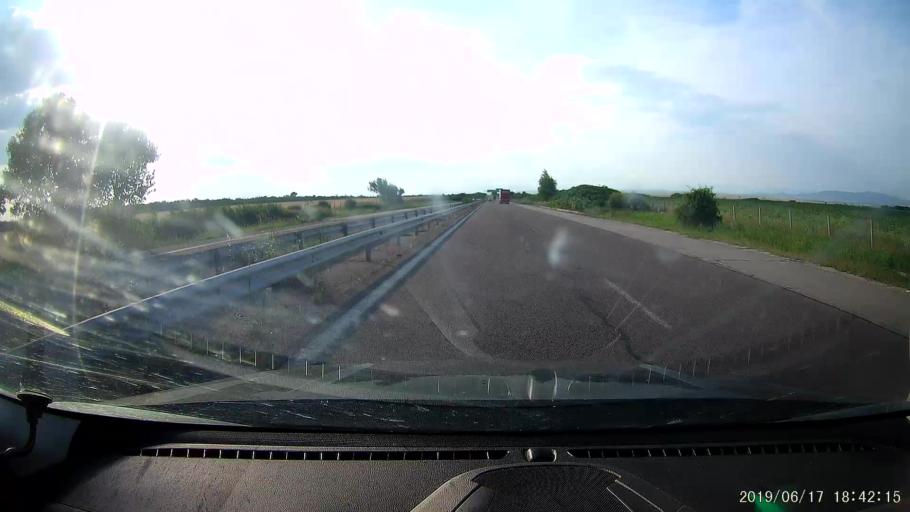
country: BG
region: Stara Zagora
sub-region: Obshtina Chirpan
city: Chirpan
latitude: 42.1879
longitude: 25.2404
